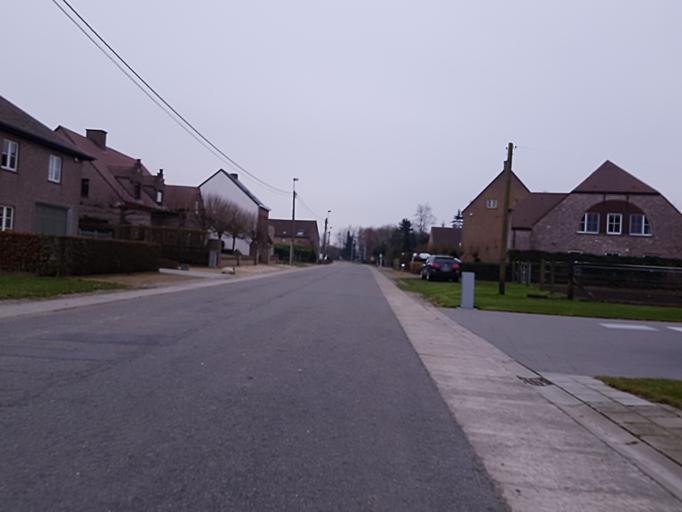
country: BE
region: Flanders
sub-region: Provincie Antwerpen
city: Willebroek
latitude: 51.0435
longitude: 4.3865
